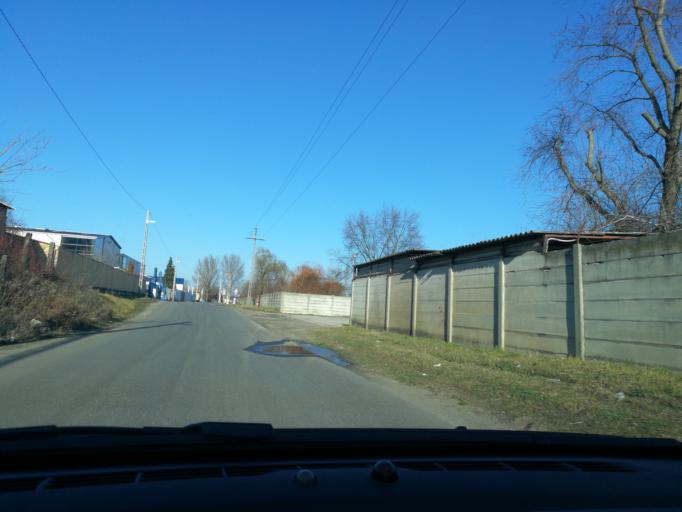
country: HU
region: Szabolcs-Szatmar-Bereg
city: Nyiregyhaza
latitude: 47.9414
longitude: 21.7465
